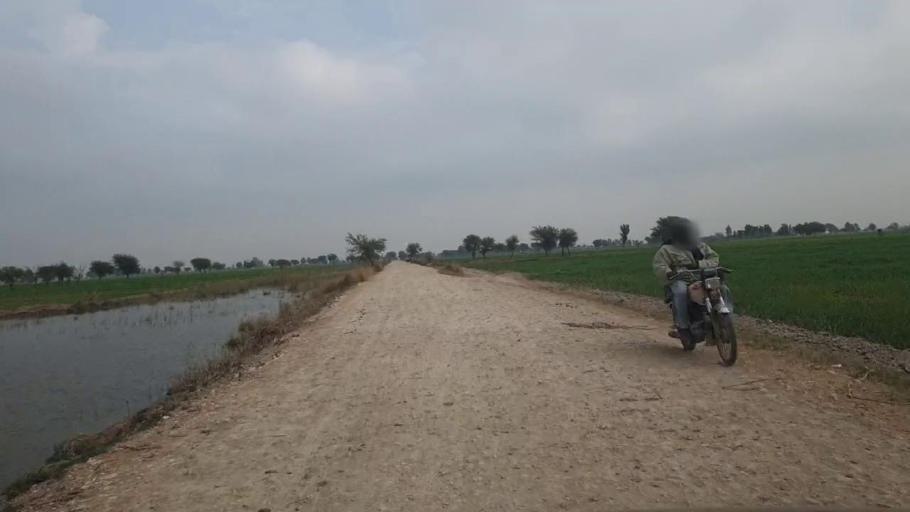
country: PK
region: Sindh
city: Shahdadpur
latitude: 25.8908
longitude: 68.6928
